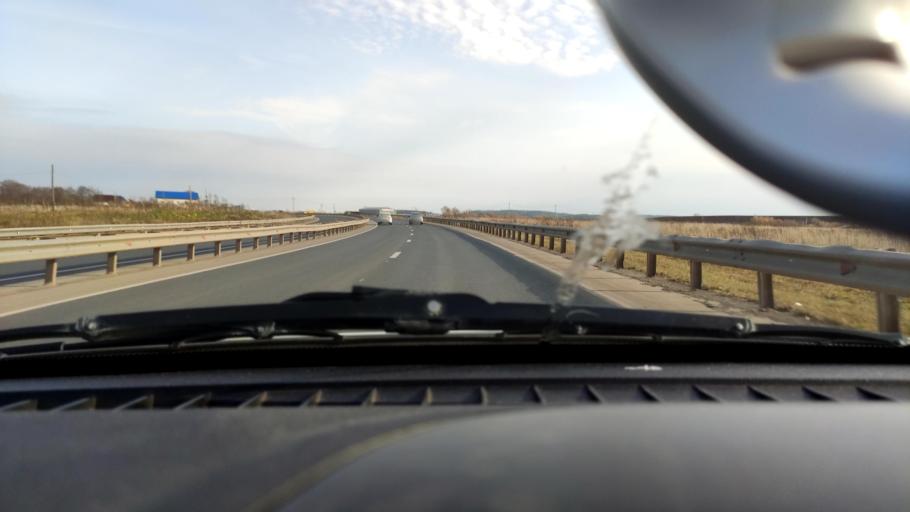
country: RU
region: Perm
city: Kultayevo
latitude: 57.8872
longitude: 55.9395
